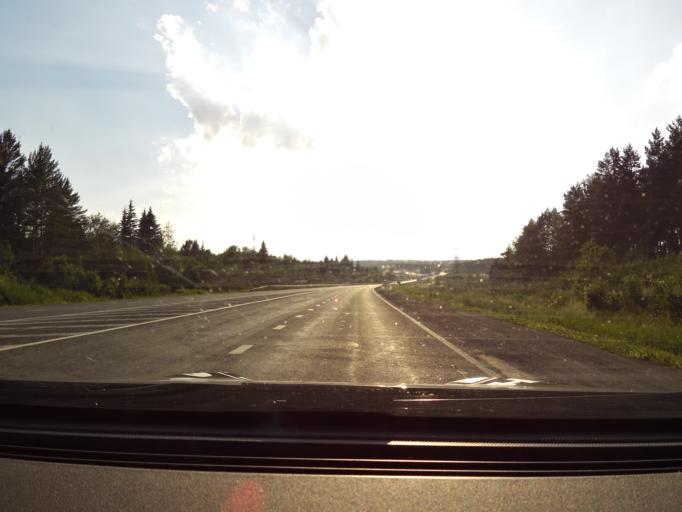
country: RU
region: Sverdlovsk
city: Revda
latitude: 56.8264
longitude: 59.8734
